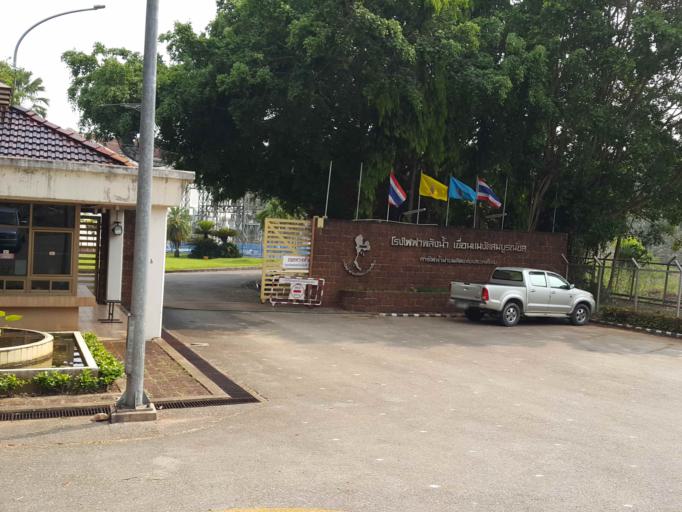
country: TH
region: Chiang Mai
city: Mae Taeng
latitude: 19.1627
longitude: 99.0355
